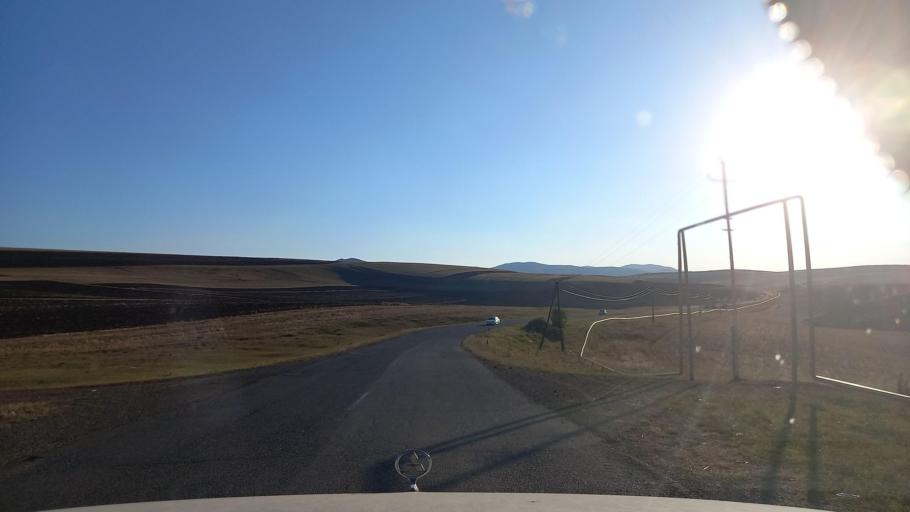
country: AZ
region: Shamkir Rayon
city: Shamkhor
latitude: 40.7645
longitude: 45.9340
